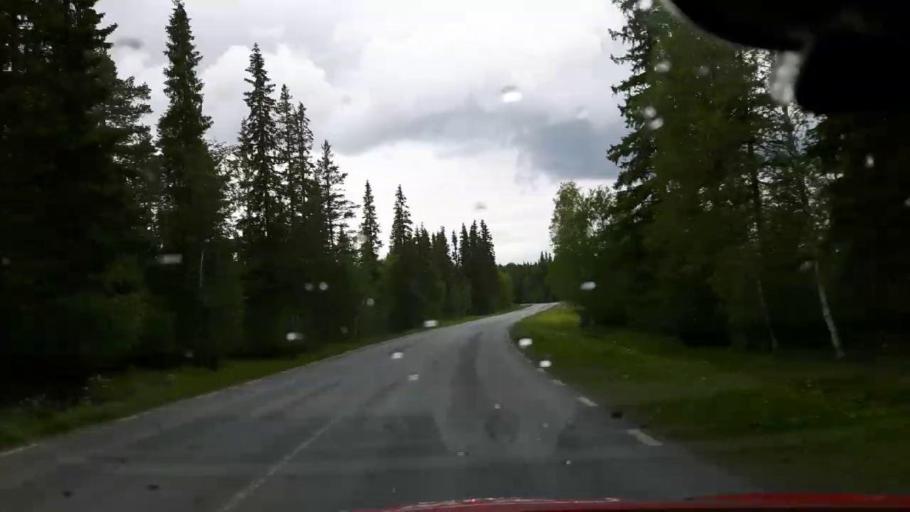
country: SE
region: Jaemtland
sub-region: Krokoms Kommun
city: Krokom
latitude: 63.4121
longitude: 14.2388
